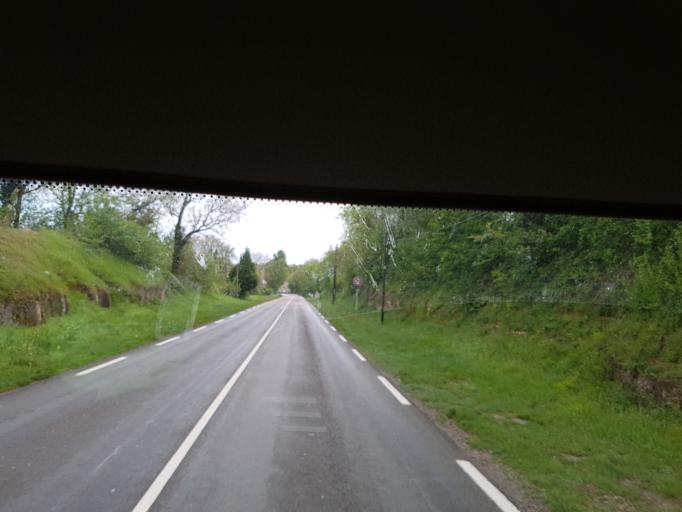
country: FR
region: Picardie
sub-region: Departement de l'Aisne
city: Coucy-le-Chateau-Auffrique
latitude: 49.4710
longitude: 3.3474
